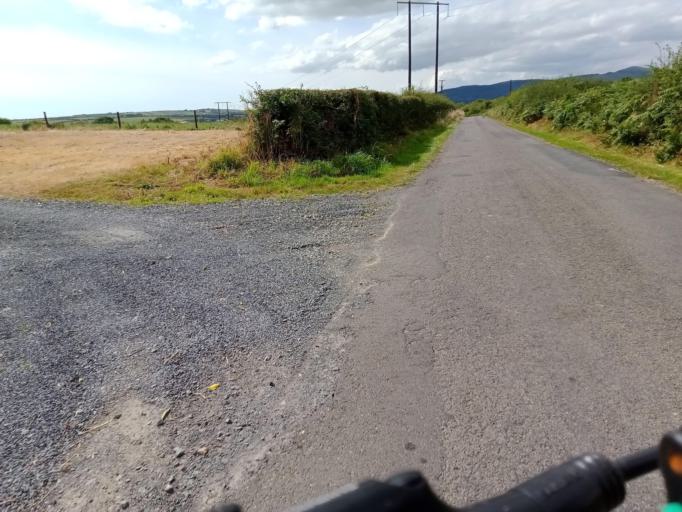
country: IE
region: Munster
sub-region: Waterford
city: Dungarvan
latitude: 52.1404
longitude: -7.4892
